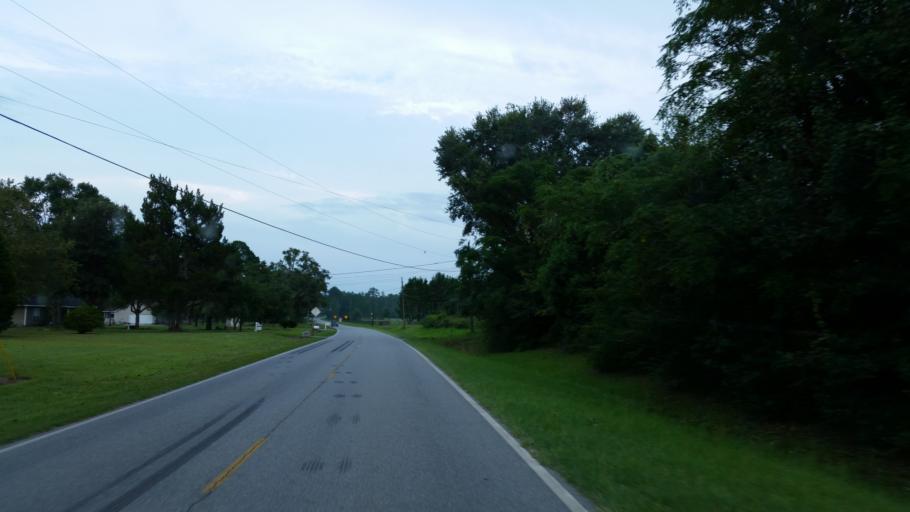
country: US
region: Georgia
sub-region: Lowndes County
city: Valdosta
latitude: 30.7623
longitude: -83.2637
